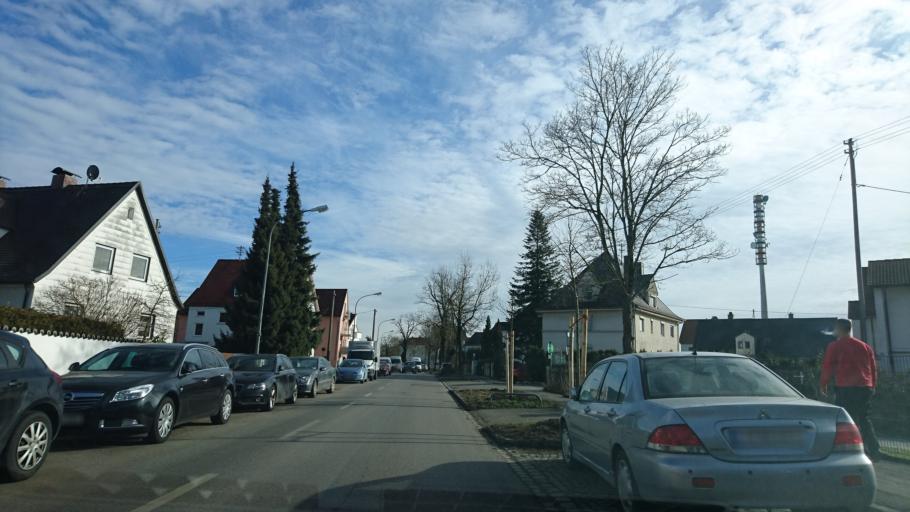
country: DE
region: Bavaria
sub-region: Swabia
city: Gersthofen
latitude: 48.3930
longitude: 10.8667
